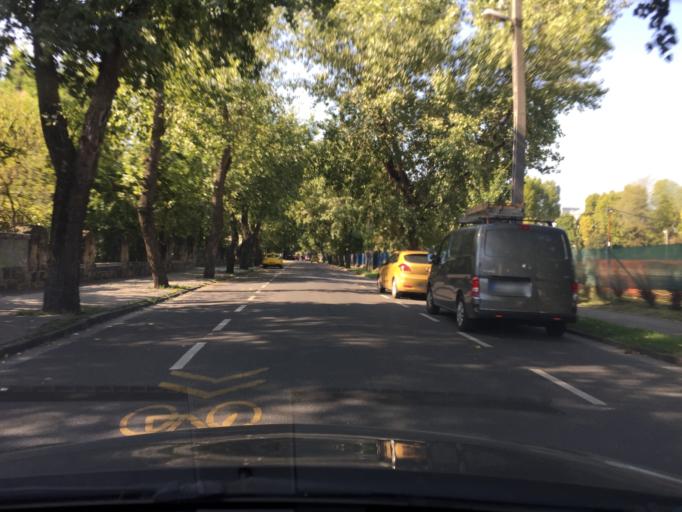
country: HU
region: Budapest
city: Budapest XIII. keruelet
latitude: 47.5219
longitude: 19.0672
